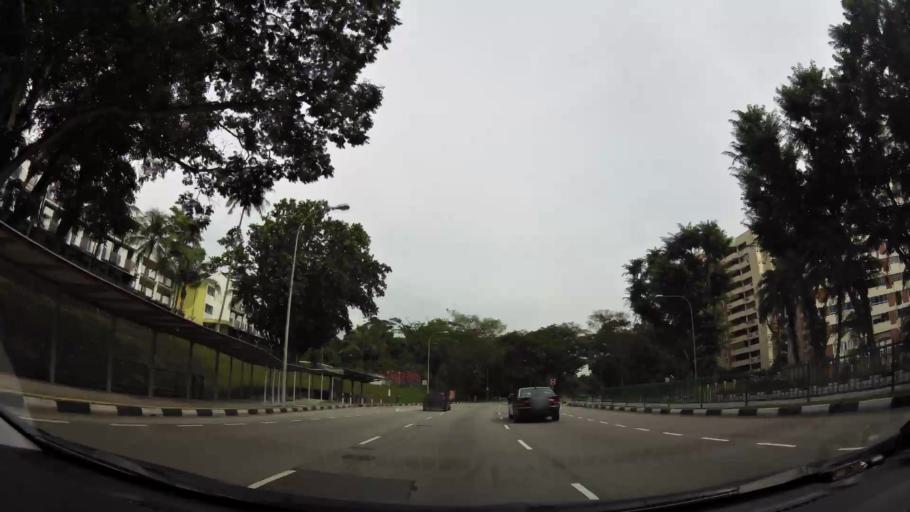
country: SG
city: Singapore
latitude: 1.3210
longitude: 103.7801
